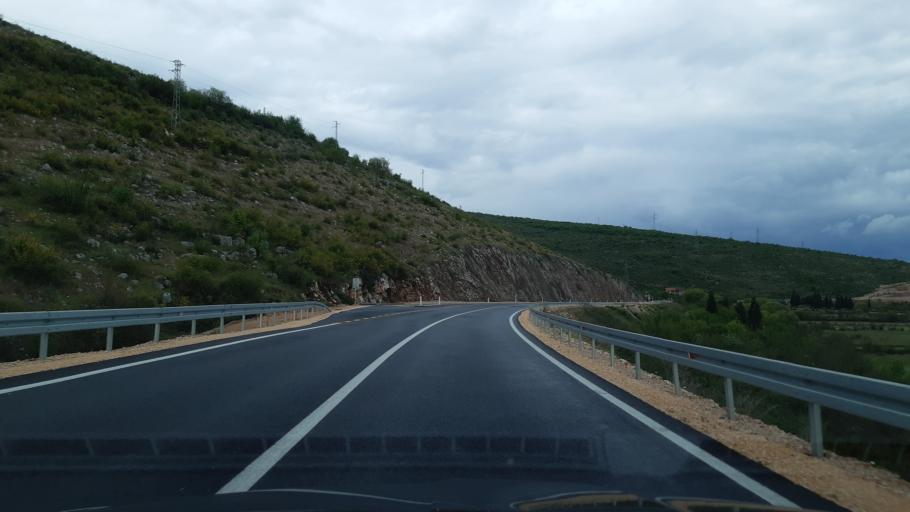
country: BA
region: Federation of Bosnia and Herzegovina
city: Ilici
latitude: 43.3329
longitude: 17.7279
